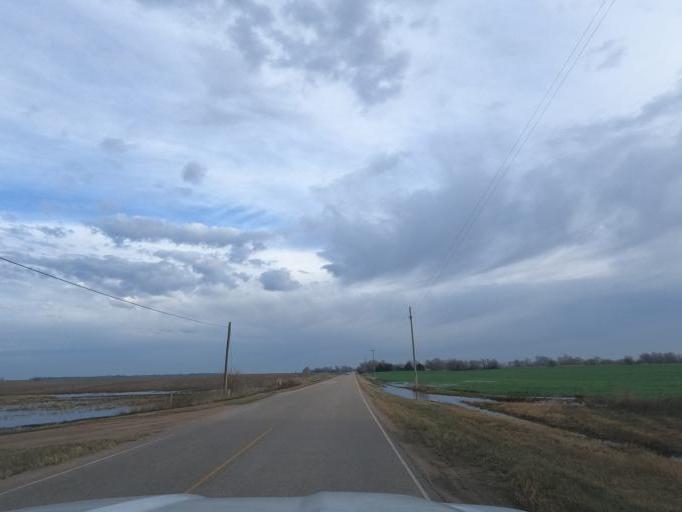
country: US
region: Kansas
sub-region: Reno County
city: South Hutchinson
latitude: 37.9705
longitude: -98.0876
